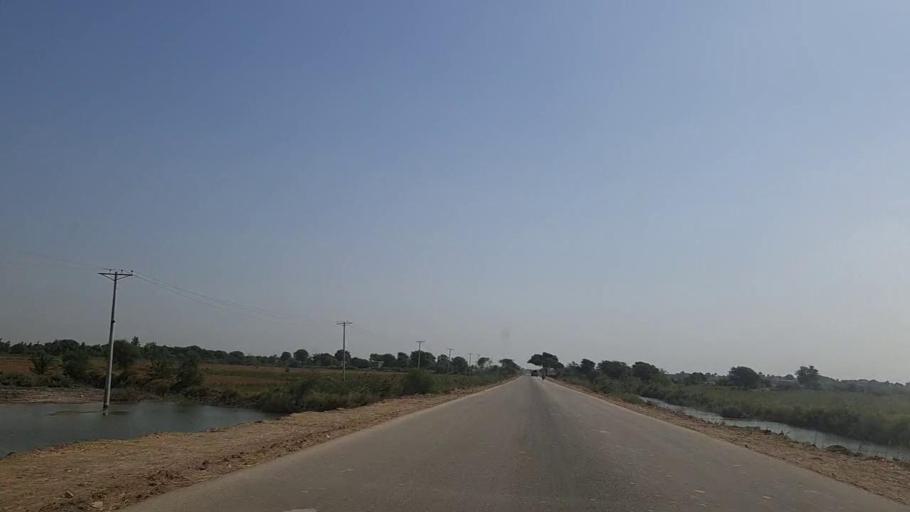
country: PK
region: Sindh
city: Daro Mehar
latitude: 24.7767
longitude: 68.2032
